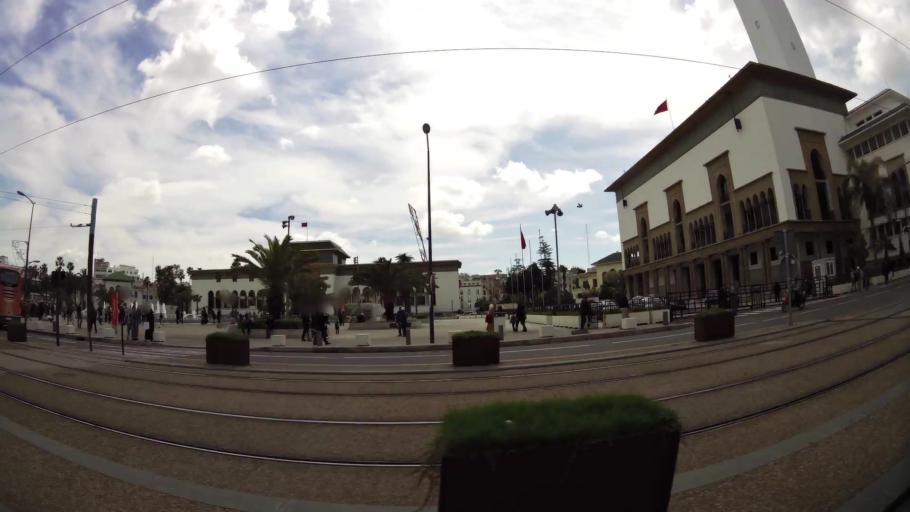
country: MA
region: Grand Casablanca
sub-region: Casablanca
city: Casablanca
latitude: 33.5910
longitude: -7.6194
